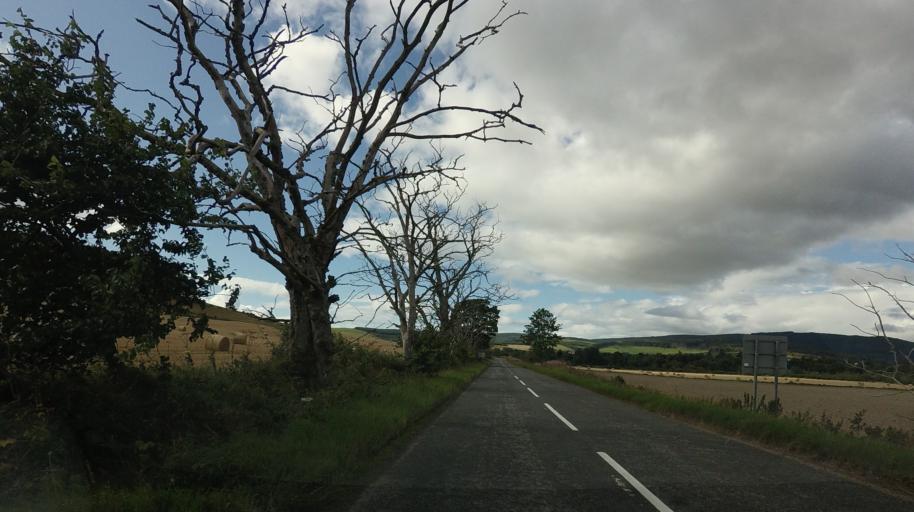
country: GB
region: Scotland
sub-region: Aberdeenshire
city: Alford
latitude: 57.2366
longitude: -2.7299
